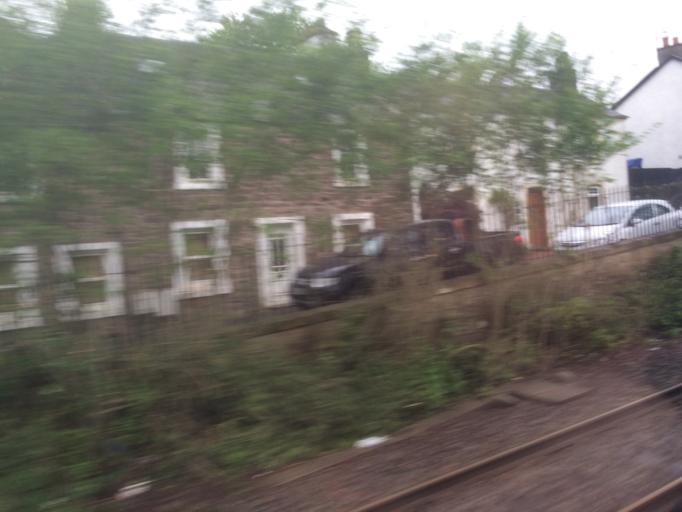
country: GB
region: Scotland
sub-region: Stirling
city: Dunblane
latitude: 56.1866
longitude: -3.9664
